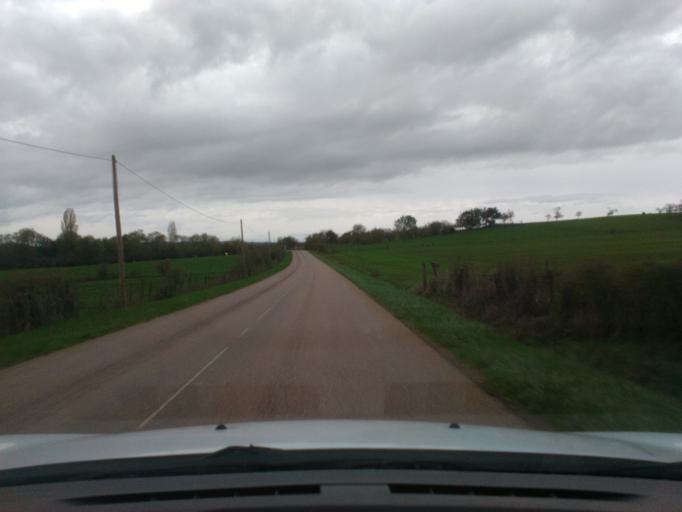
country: FR
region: Lorraine
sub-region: Departement des Vosges
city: Mirecourt
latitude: 48.3496
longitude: 6.0941
